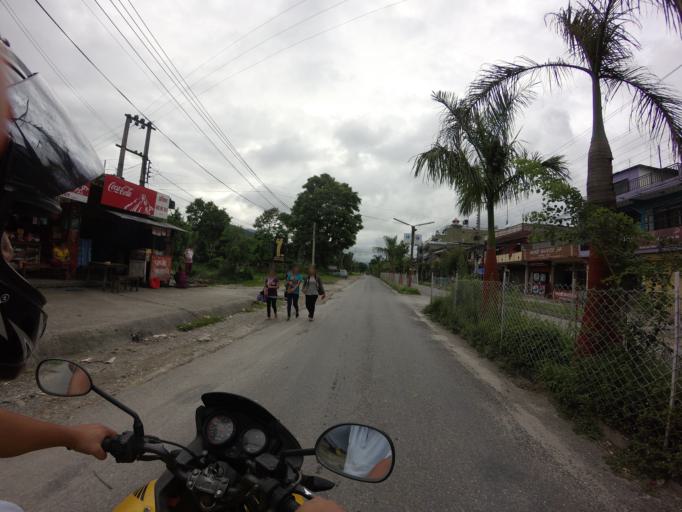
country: NP
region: Western Region
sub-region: Gandaki Zone
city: Pokhara
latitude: 28.1990
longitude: 83.9746
